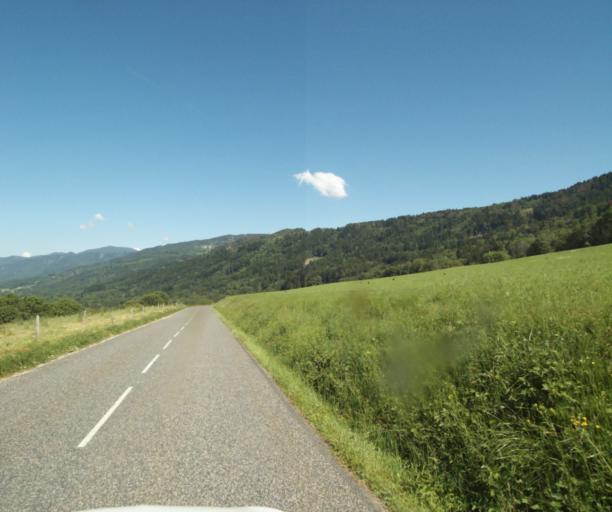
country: FR
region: Rhone-Alpes
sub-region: Departement de la Haute-Savoie
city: Bons-en-Chablais
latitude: 46.2522
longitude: 6.3685
